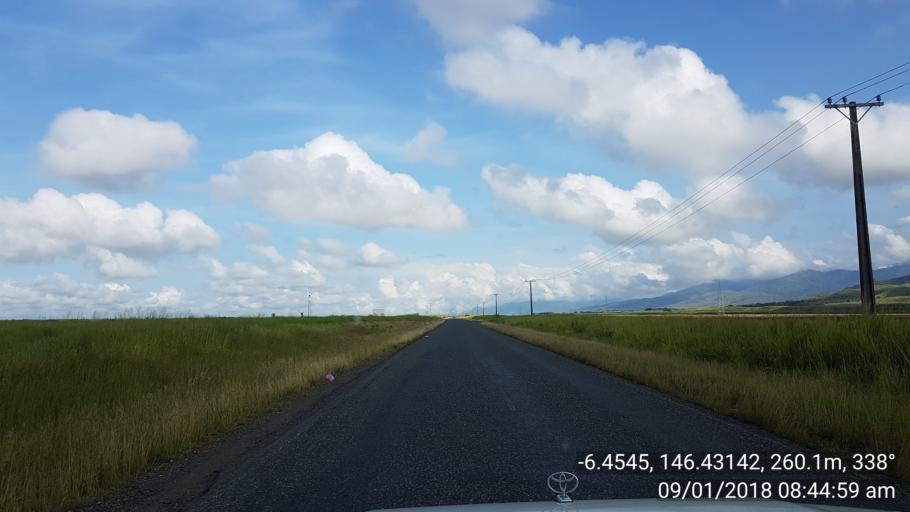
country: PG
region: Eastern Highlands
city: Kainantu
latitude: -6.4542
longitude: 146.4314
